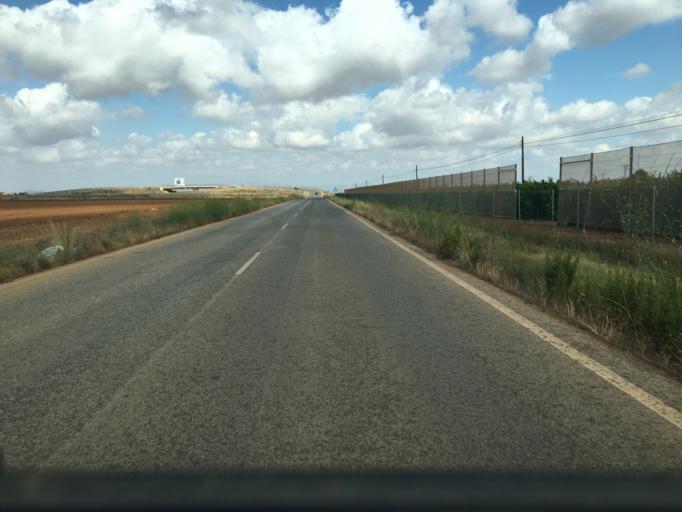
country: ES
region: Murcia
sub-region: Murcia
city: La Union
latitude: 37.6492
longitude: -0.8791
